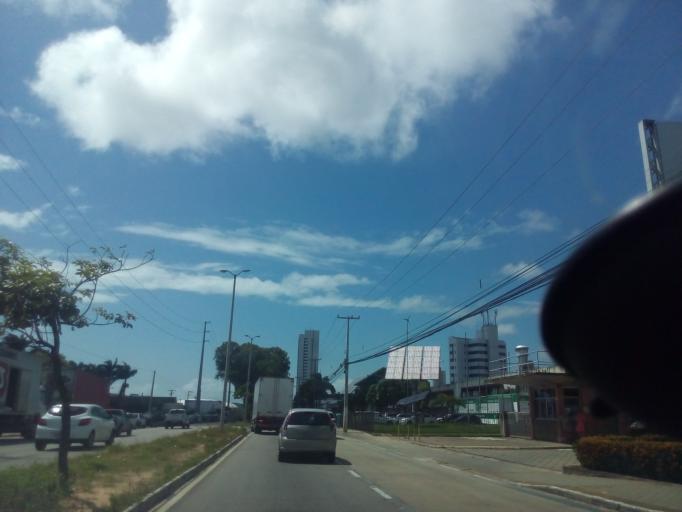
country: BR
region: Rio Grande do Norte
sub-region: Natal
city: Natal
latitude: -5.8238
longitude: -35.2264
